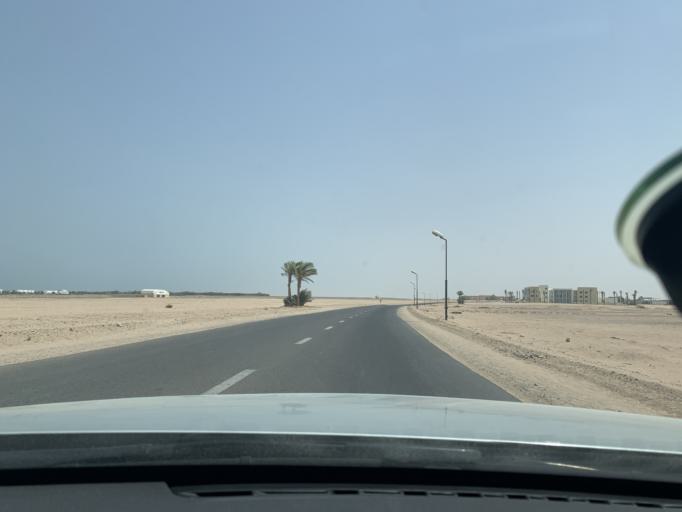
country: EG
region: Red Sea
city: El Gouna
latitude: 27.3730
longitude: 33.6621
